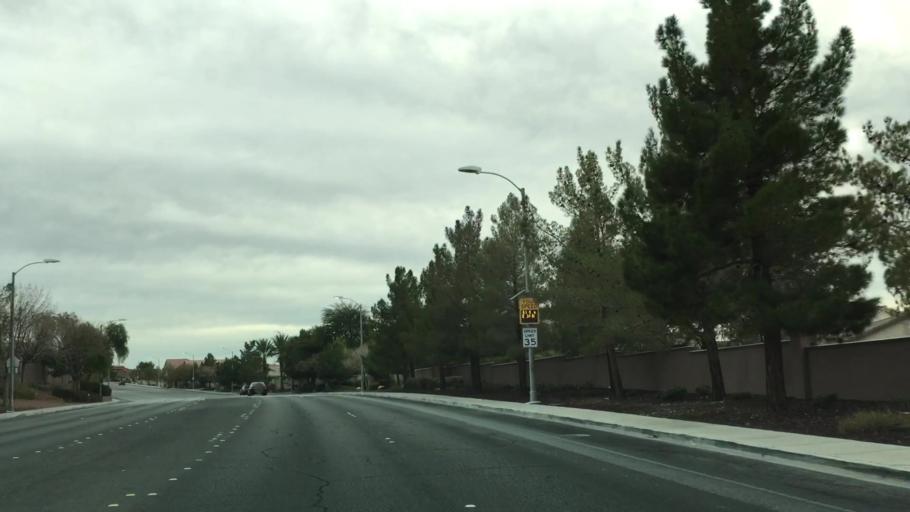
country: US
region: Nevada
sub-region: Clark County
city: Whitney
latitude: 36.0118
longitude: -115.0953
